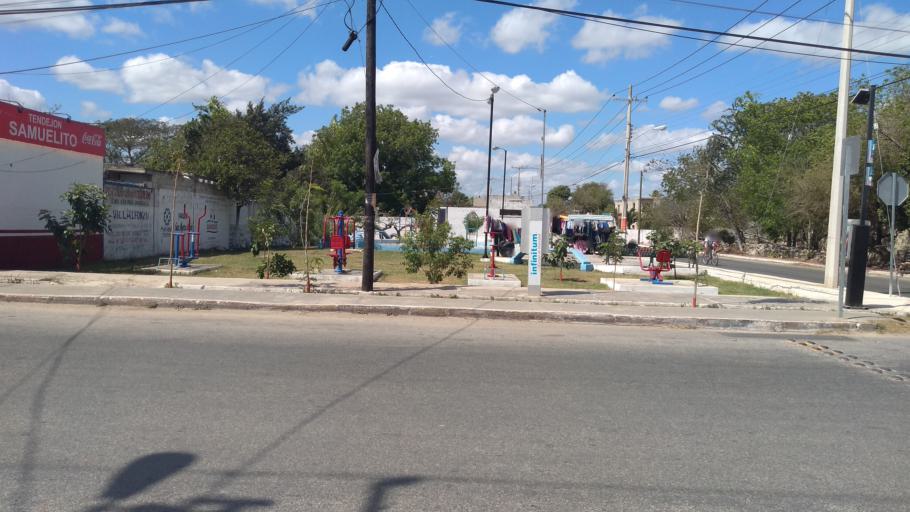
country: MX
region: Yucatan
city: Itzincab Palomeque
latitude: 20.9269
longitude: -89.6735
